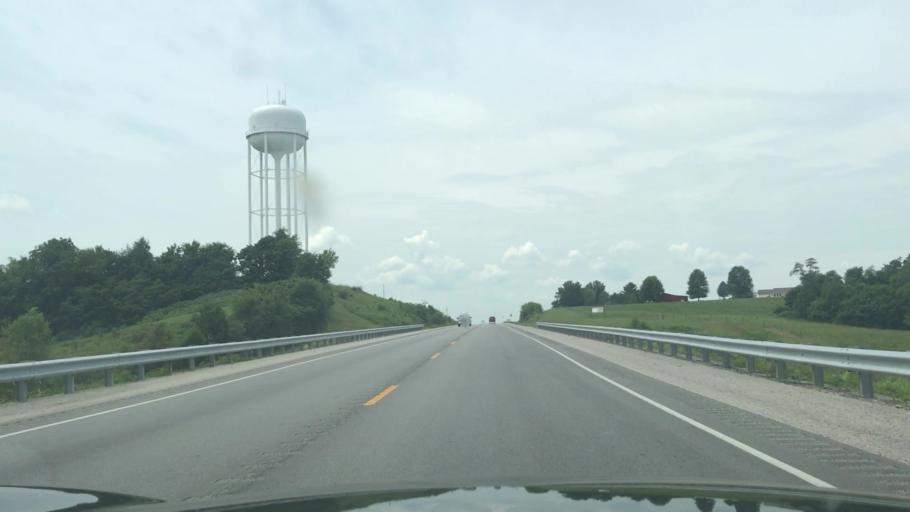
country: US
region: Kentucky
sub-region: Green County
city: Greensburg
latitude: 37.3089
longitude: -85.4320
